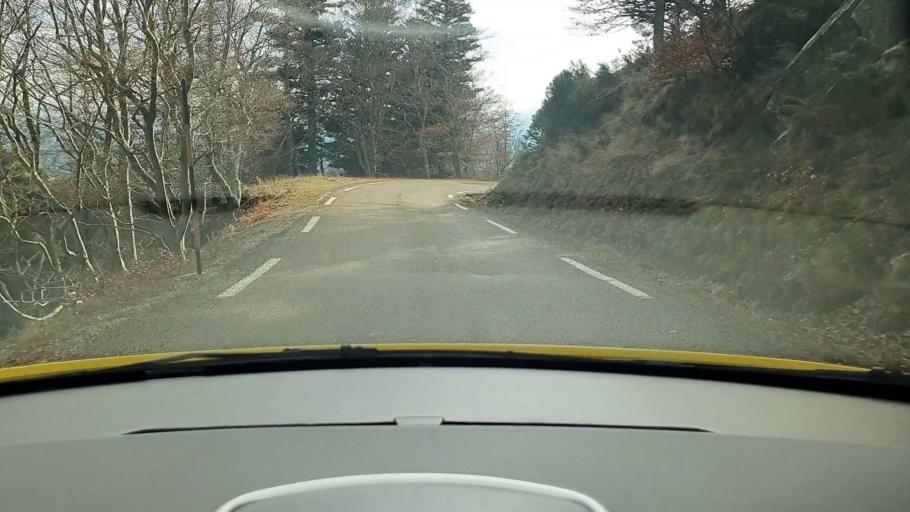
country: FR
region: Languedoc-Roussillon
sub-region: Departement du Gard
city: Branoux-les-Taillades
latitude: 44.3646
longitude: 3.9162
